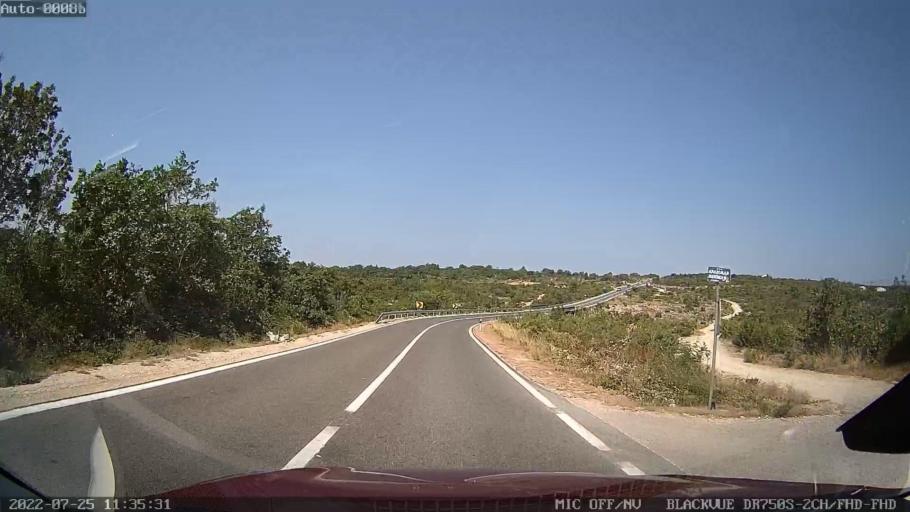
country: HR
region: Zadarska
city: Policnik
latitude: 44.2338
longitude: 15.4074
